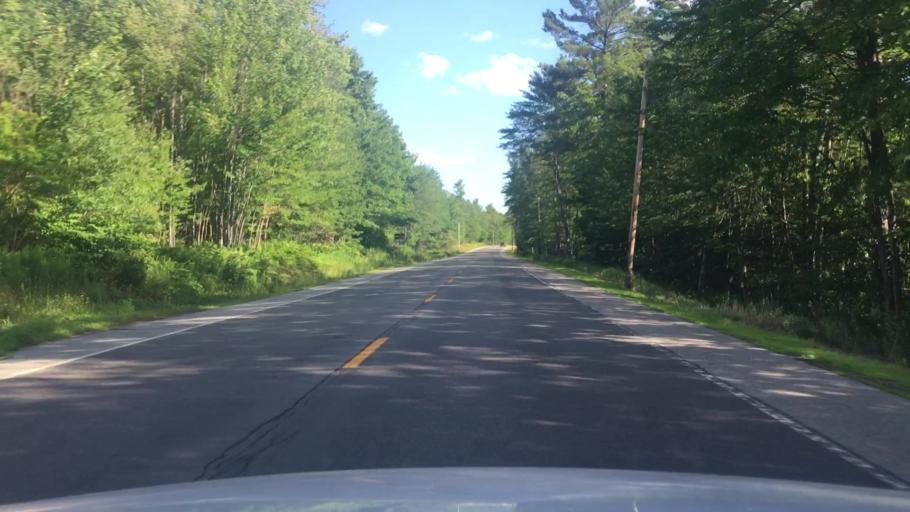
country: US
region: Maine
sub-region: Franklin County
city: Jay
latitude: 44.5417
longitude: -70.2358
